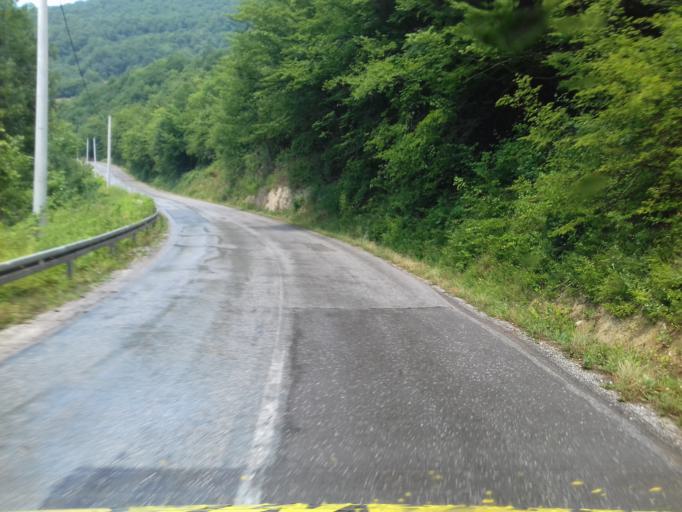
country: BA
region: Federation of Bosnia and Herzegovina
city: Kiseljak
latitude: 43.9556
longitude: 18.1103
